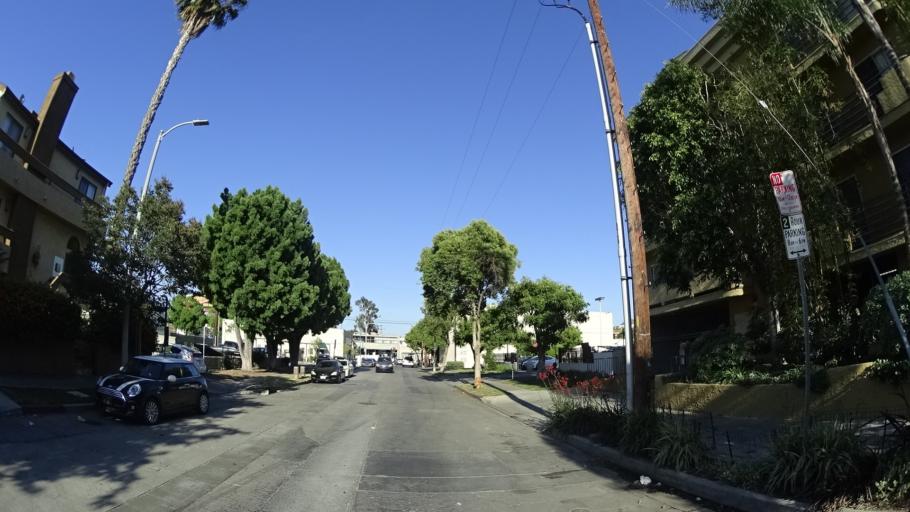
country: US
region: California
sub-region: Los Angeles County
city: North Hollywood
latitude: 34.1619
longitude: -118.3740
